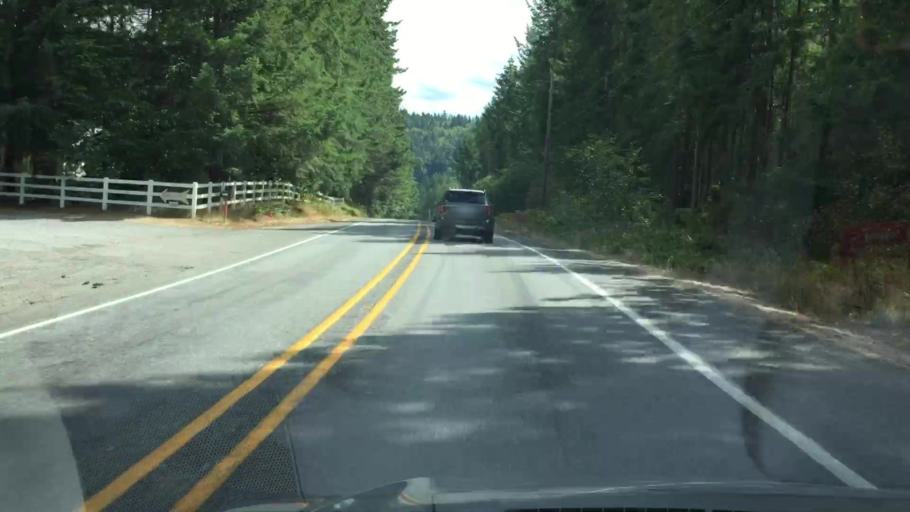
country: US
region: Washington
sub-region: Pierce County
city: Eatonville
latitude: 46.8776
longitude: -122.3023
